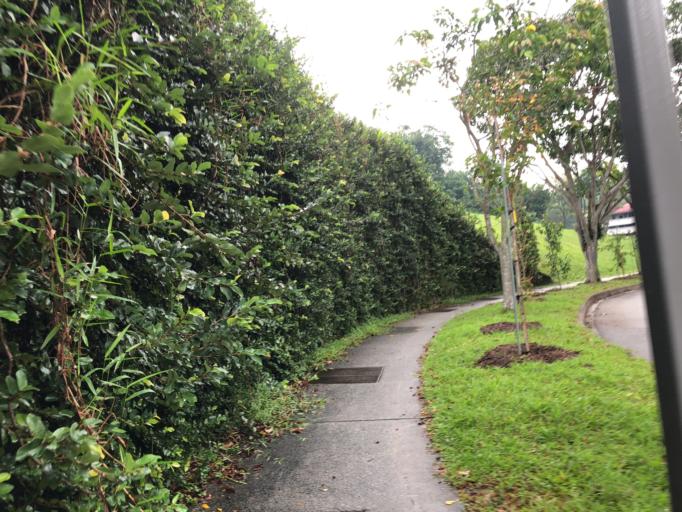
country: MY
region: Johor
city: Johor Bahru
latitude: 1.3556
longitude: 103.7495
